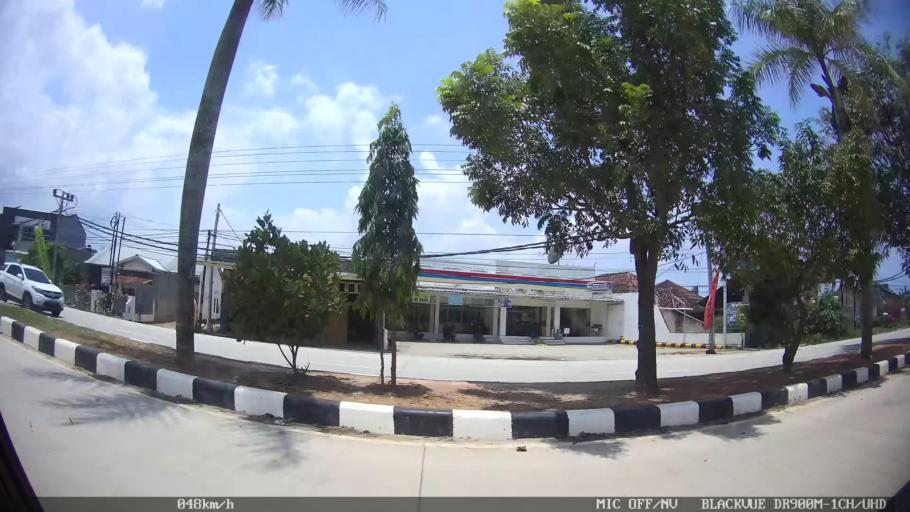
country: ID
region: Lampung
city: Kedaton
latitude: -5.3768
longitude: 105.2945
